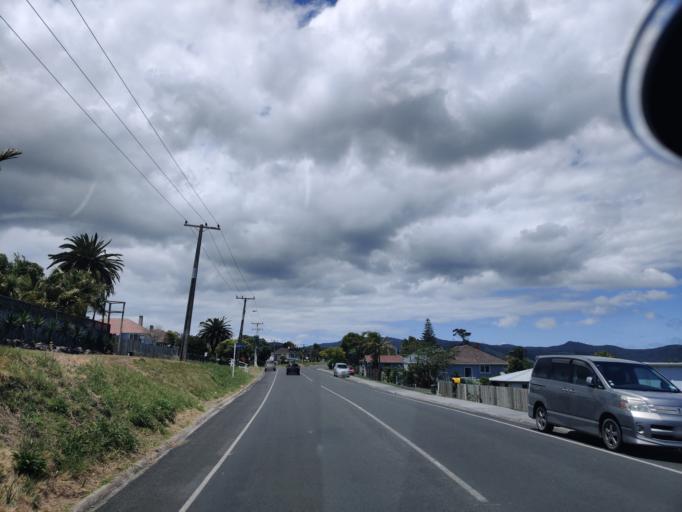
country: NZ
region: Northland
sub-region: Far North District
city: Kaitaia
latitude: -35.1159
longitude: 173.2576
